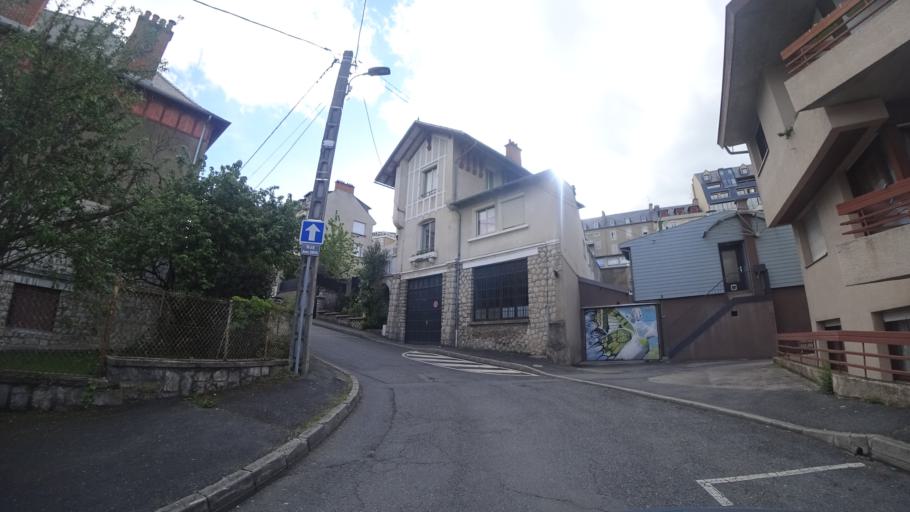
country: FR
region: Midi-Pyrenees
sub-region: Departement de l'Aveyron
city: Rodez
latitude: 44.3499
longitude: 2.5792
